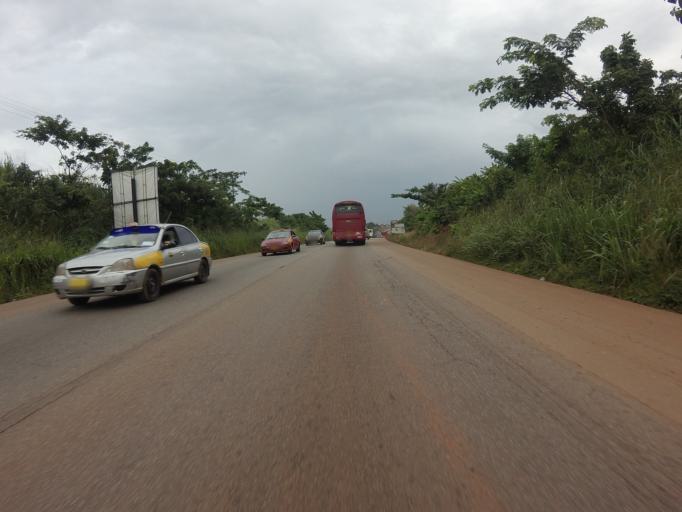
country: GH
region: Ashanti
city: Konongo
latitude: 6.6179
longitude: -1.1891
